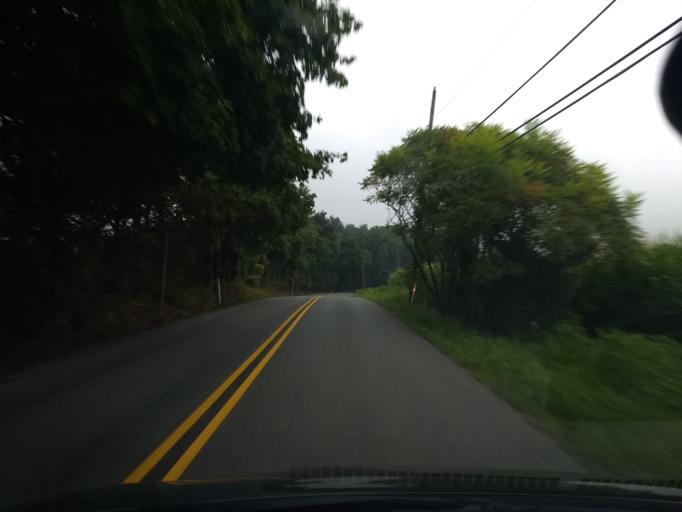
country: US
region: Pennsylvania
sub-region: Westmoreland County
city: Greensburg
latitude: 40.3459
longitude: -79.5052
